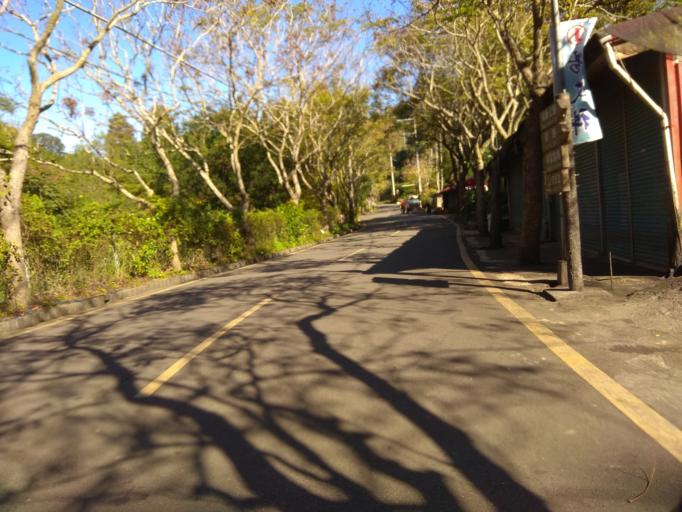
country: TW
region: Taiwan
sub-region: Hsinchu
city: Zhubei
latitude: 24.8581
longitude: 121.1052
